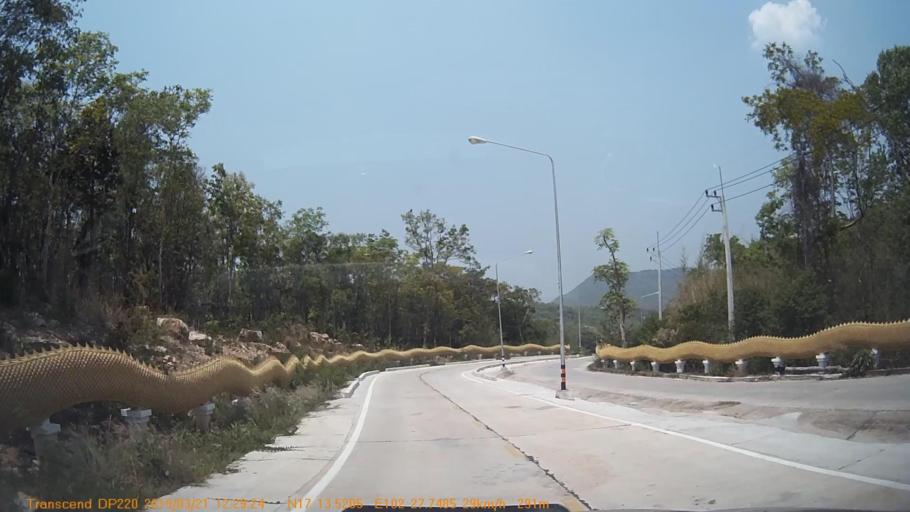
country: TH
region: Changwat Nong Bua Lamphu
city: Nong Bua Lamphu
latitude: 17.2254
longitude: 102.4625
